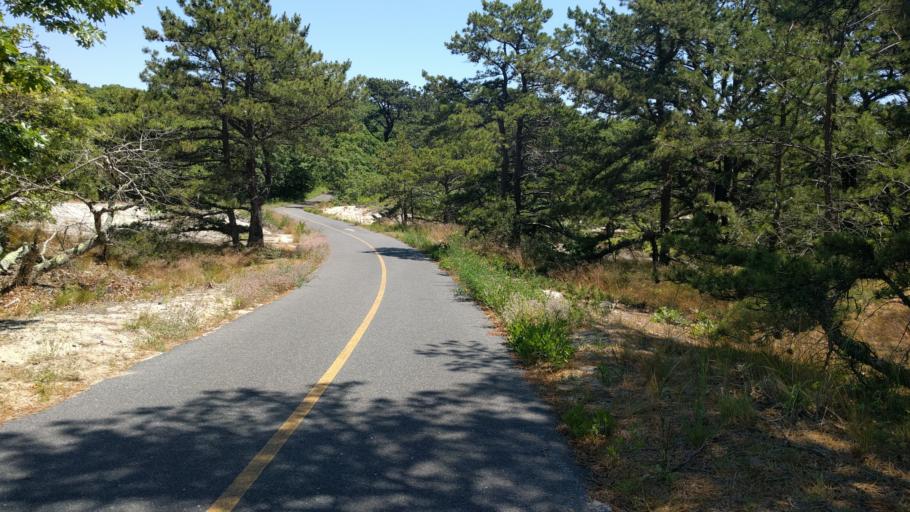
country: US
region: Massachusetts
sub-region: Barnstable County
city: Provincetown
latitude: 42.0598
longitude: -70.2120
